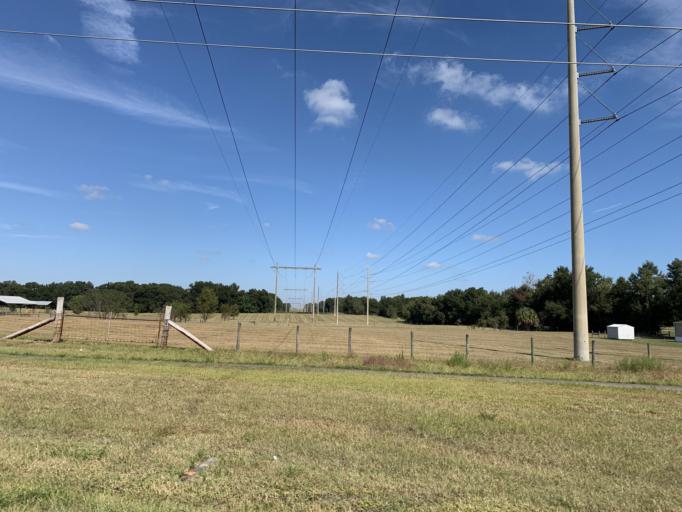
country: US
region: Florida
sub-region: Marion County
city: Ocala
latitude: 29.1643
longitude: -82.0752
